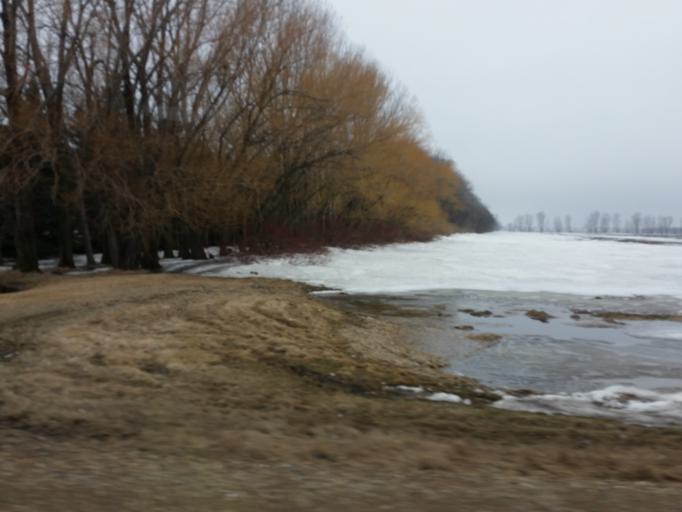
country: US
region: North Dakota
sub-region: Walsh County
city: Grafton
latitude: 48.6085
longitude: -97.4480
